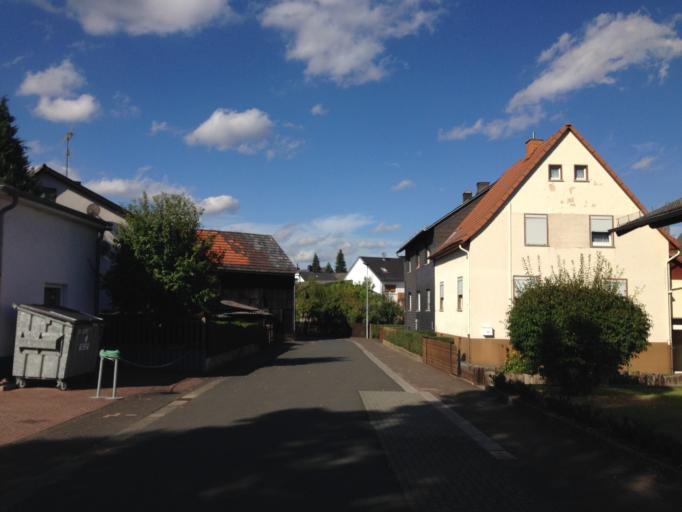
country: DE
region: Hesse
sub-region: Regierungsbezirk Giessen
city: Bischoffen
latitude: 50.6728
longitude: 8.5248
